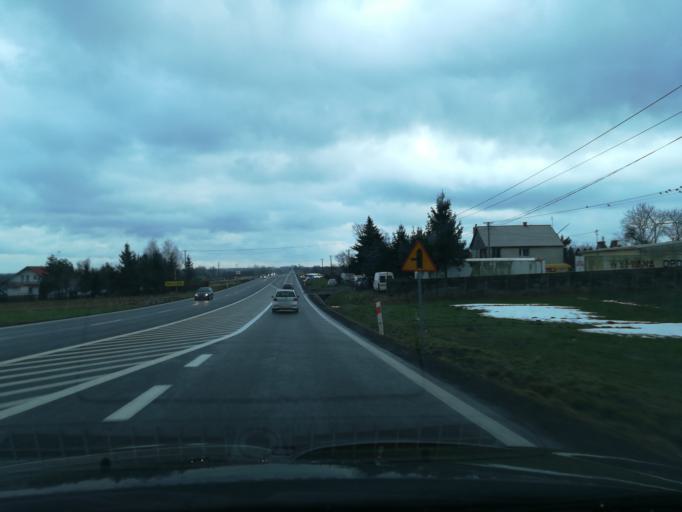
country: PL
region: Subcarpathian Voivodeship
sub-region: Powiat lancucki
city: Gluchow
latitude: 50.0787
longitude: 22.2876
